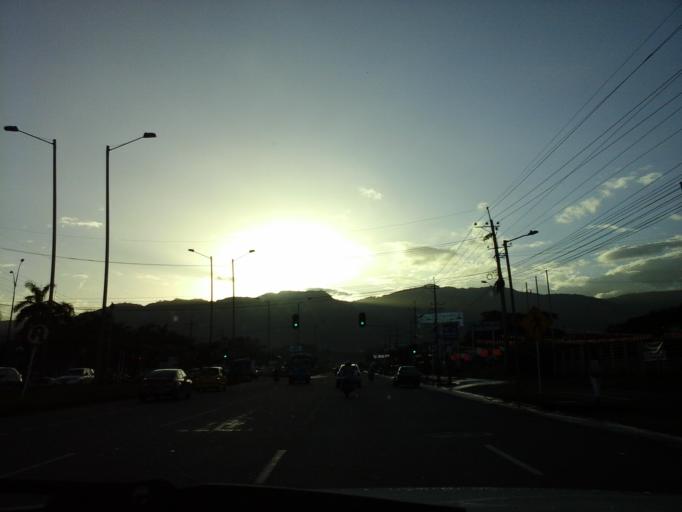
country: CO
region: Meta
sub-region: Villavicencio
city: Villavicencio
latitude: 4.1154
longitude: -73.6333
